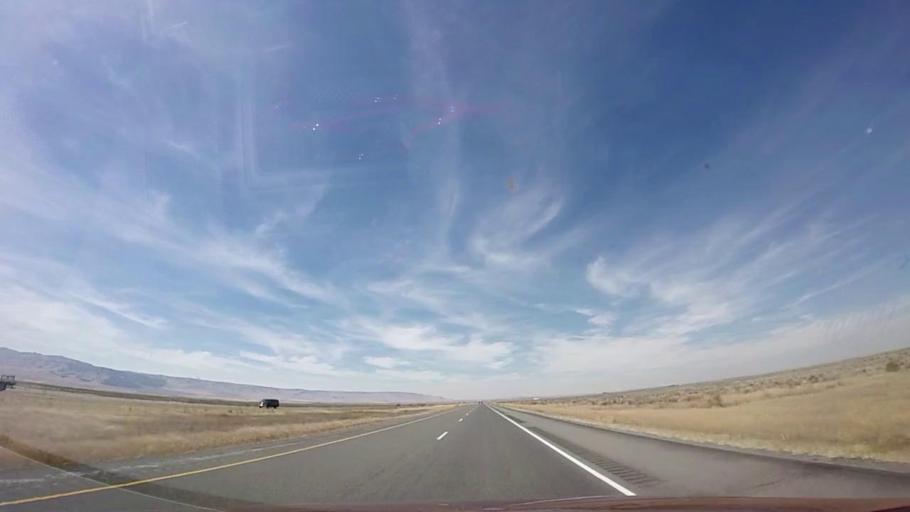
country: US
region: Idaho
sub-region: Minidoka County
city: Rupert
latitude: 42.3725
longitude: -113.2690
